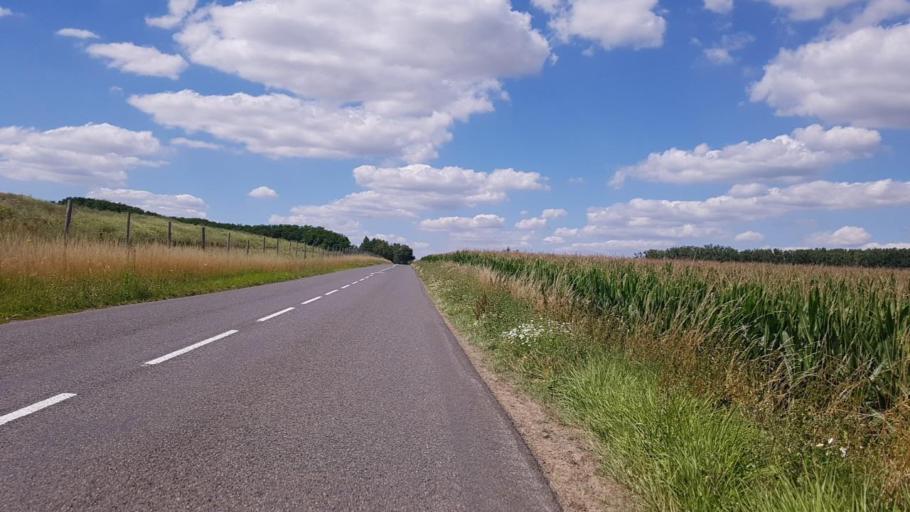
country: FR
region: Ile-de-France
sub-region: Departement de Seine-et-Marne
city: Moussy-le-Vieux
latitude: 49.0248
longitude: 2.6436
